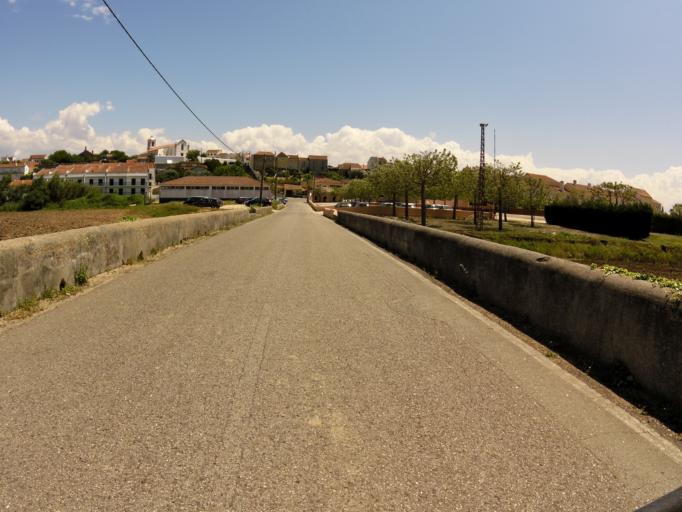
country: PT
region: Coimbra
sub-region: Montemor-O-Velho
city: Montemor-o-Velho
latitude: 40.1739
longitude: -8.6887
